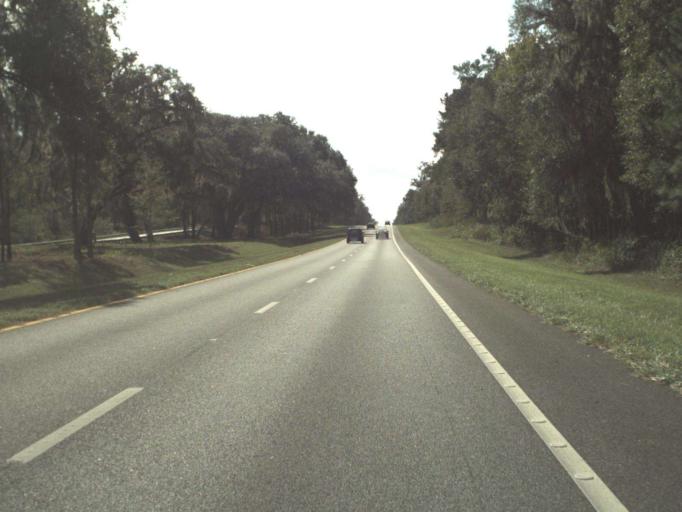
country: US
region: Florida
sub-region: Leon County
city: Tallahassee
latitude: 30.6378
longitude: -84.1692
